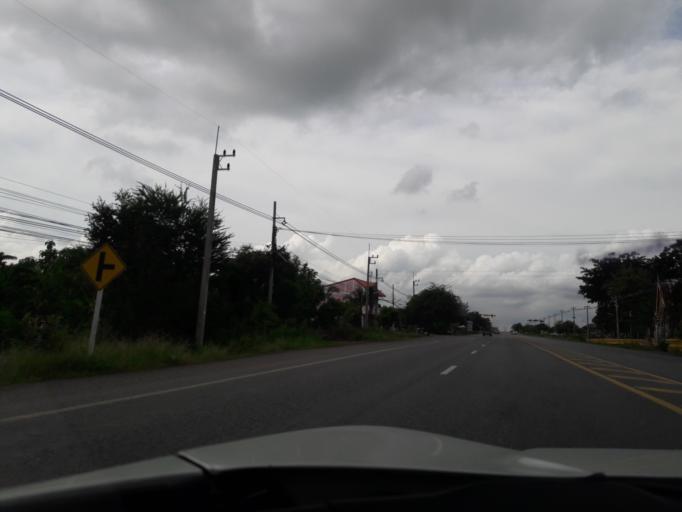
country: TH
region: Lop Buri
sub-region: Amphoe Tha Luang
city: Tha Luang
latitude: 15.0791
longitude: 101.0278
